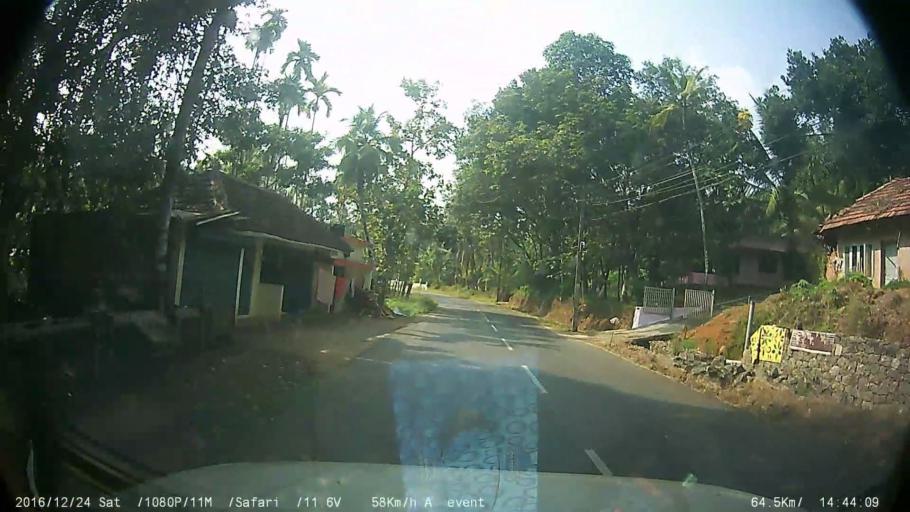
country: IN
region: Kerala
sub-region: Kottayam
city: Lalam
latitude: 9.7767
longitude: 76.7225
